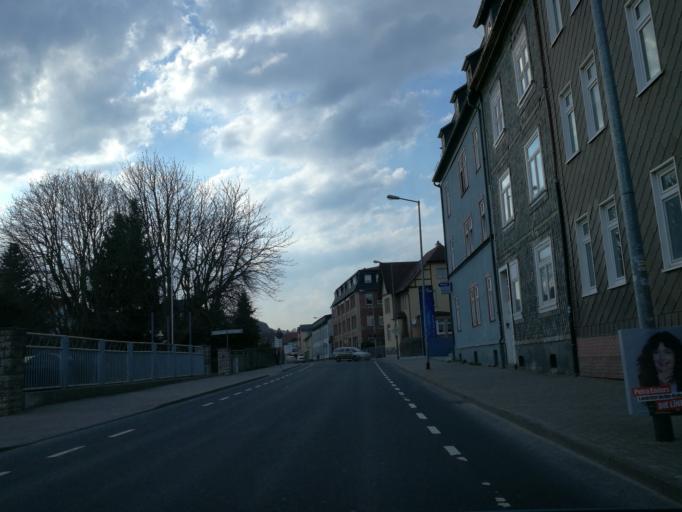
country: DE
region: Thuringia
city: Ilmenau
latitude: 50.6824
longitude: 10.9253
